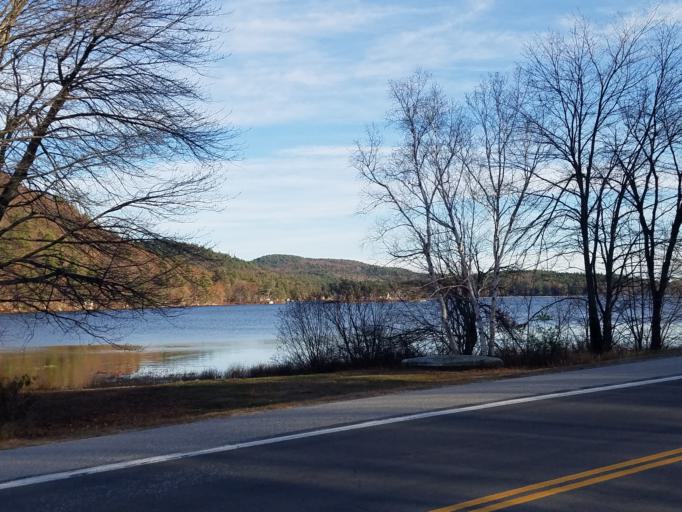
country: US
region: New Hampshire
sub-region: Merrimack County
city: Sutton
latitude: 43.2489
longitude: -71.9245
